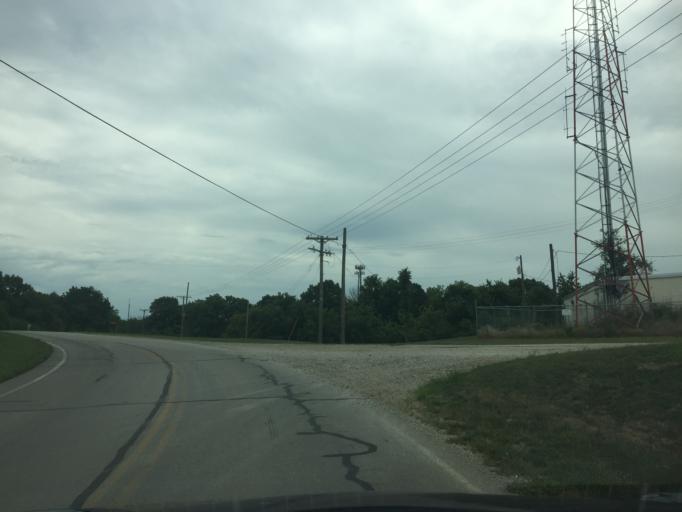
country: US
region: Kansas
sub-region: Leavenworth County
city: Leavenworth
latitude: 39.3609
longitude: -94.9383
